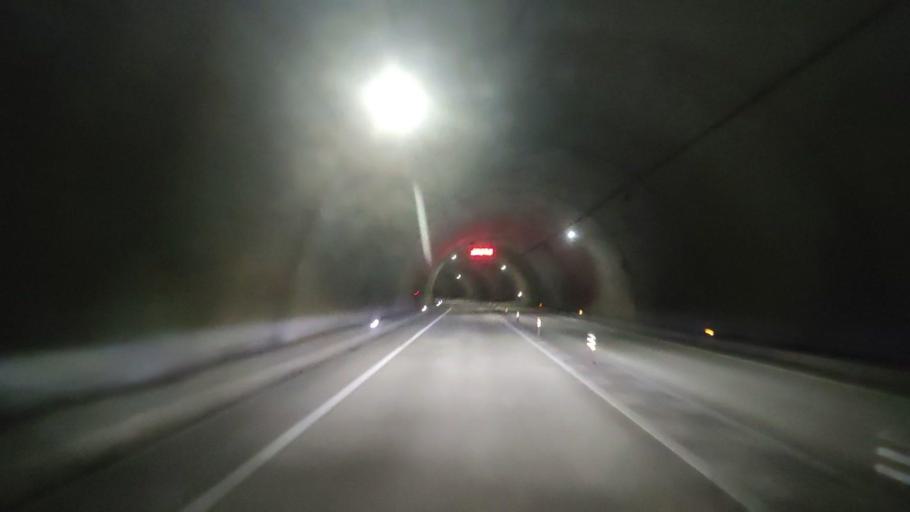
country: JP
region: Wakayama
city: Shingu
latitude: 33.7198
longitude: 135.9767
